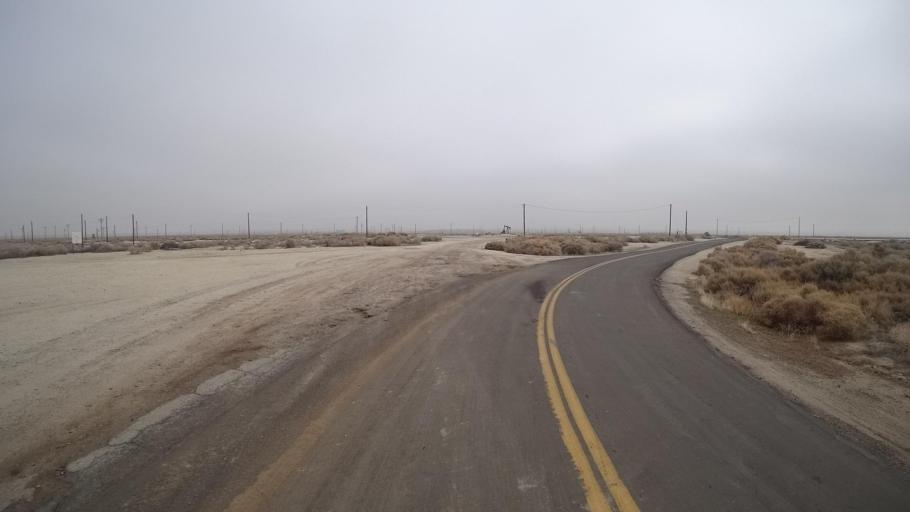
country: US
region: California
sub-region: Kern County
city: Maricopa
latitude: 35.0785
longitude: -119.3793
